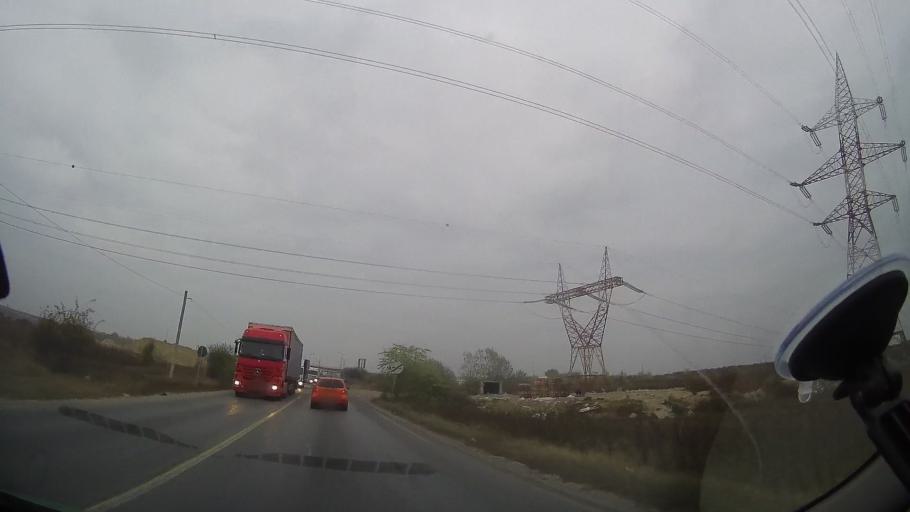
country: RO
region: Ilfov
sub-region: Comuna Glina
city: Catelu
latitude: 44.4032
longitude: 26.2315
